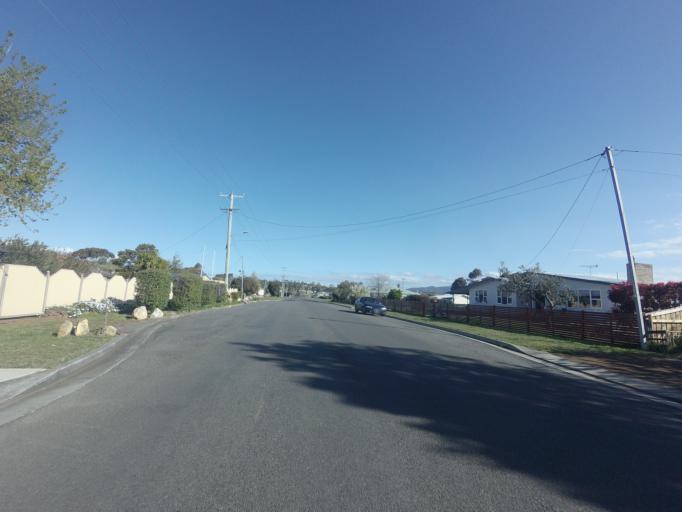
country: AU
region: Tasmania
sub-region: Sorell
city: Sorell
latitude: -42.5067
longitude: 147.9163
